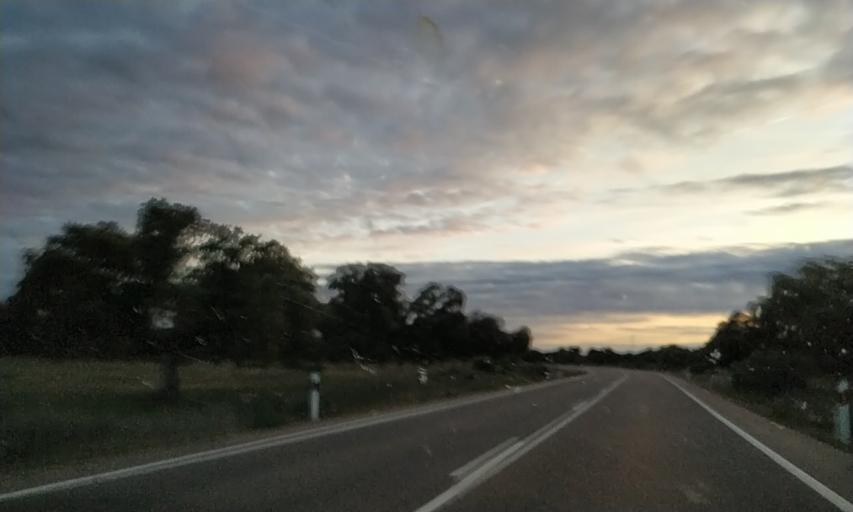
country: ES
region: Extremadura
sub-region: Provincia de Badajoz
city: Villar del Rey
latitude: 39.0392
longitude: -6.8141
